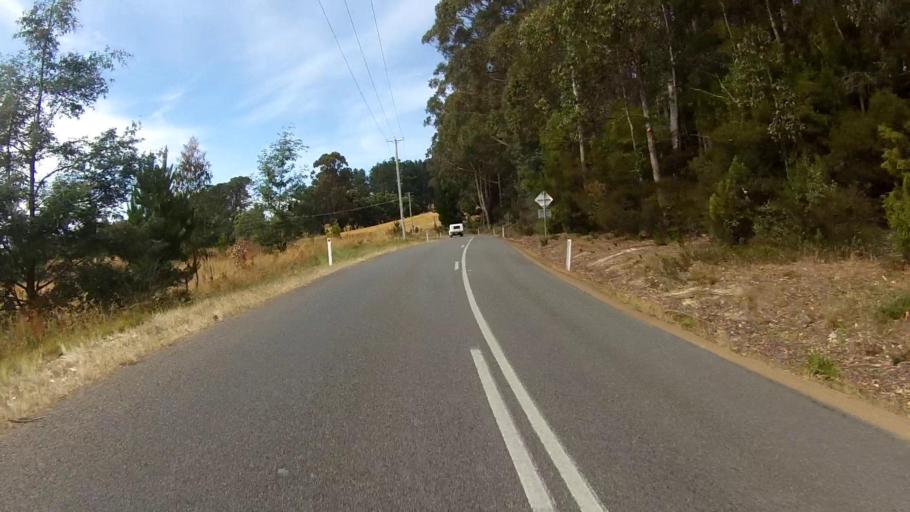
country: AU
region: Tasmania
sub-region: Kingborough
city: Kettering
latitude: -43.1924
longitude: 147.2475
